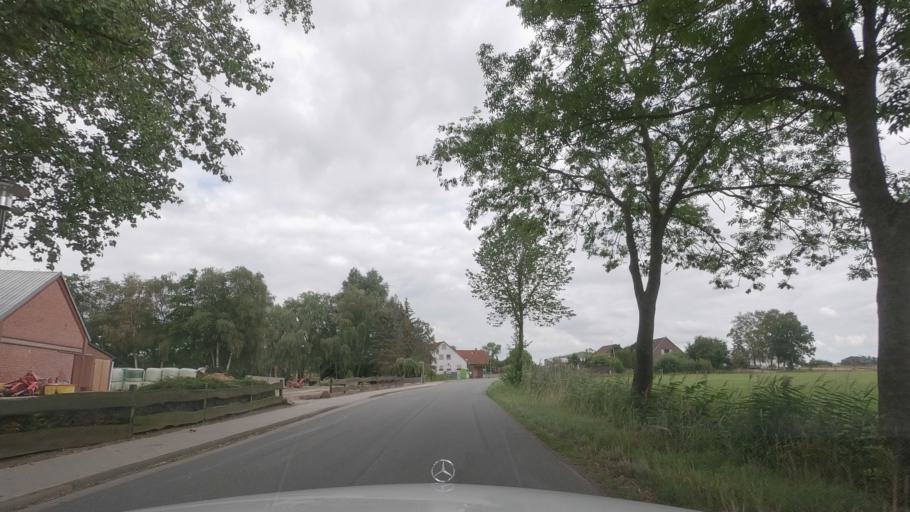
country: DE
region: Lower Saxony
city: Uthlede
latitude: 53.2947
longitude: 8.5300
